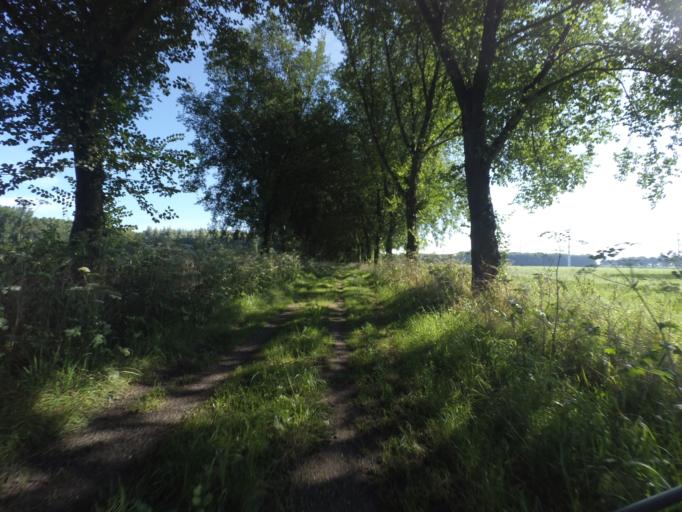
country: NL
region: Flevoland
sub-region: Gemeente Zeewolde
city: Zeewolde
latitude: 52.3980
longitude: 5.4947
